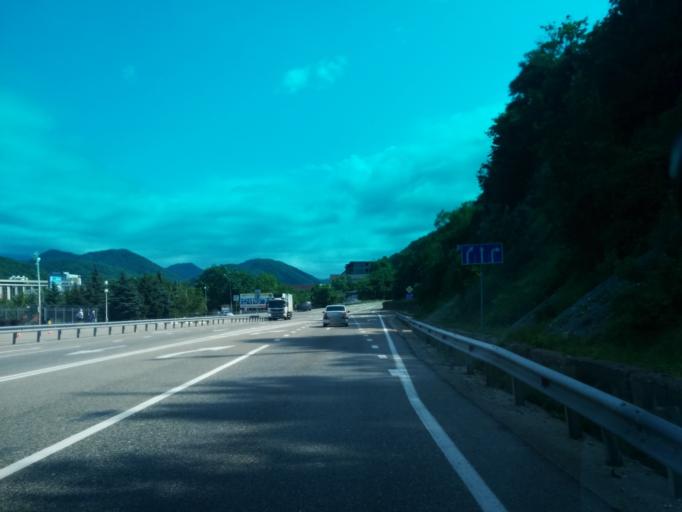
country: RU
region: Krasnodarskiy
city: Nebug
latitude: 44.1628
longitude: 39.0017
